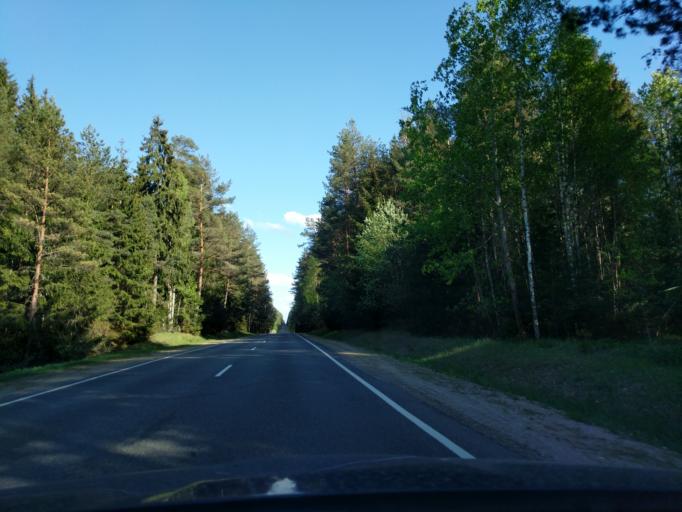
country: BY
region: Minsk
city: Myadzyel
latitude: 54.8059
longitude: 26.9911
